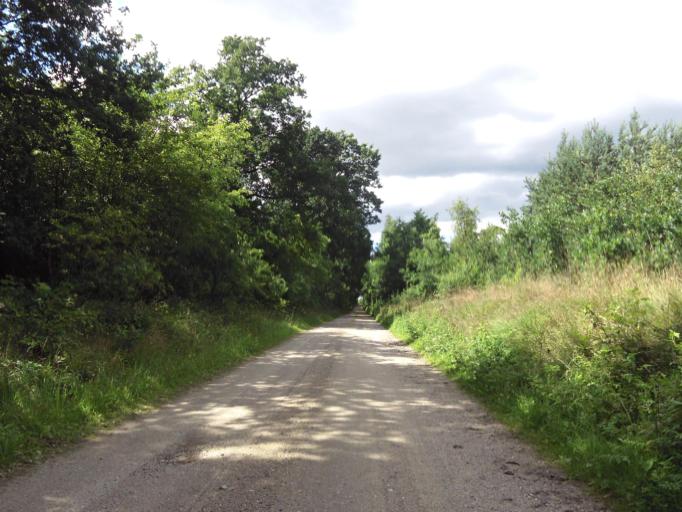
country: DK
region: South Denmark
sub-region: Haderslev Kommune
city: Vojens
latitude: 55.3241
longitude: 9.1950
